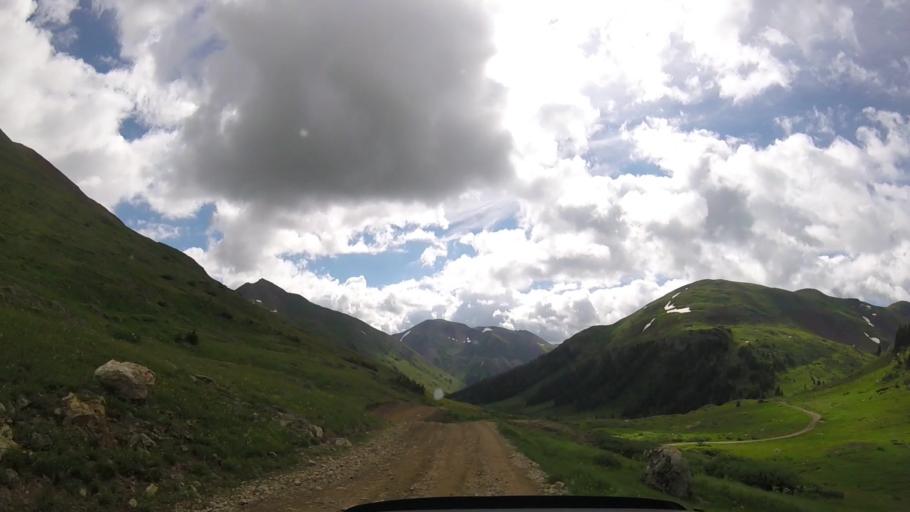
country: US
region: Colorado
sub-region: Ouray County
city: Ouray
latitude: 37.9324
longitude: -107.5932
